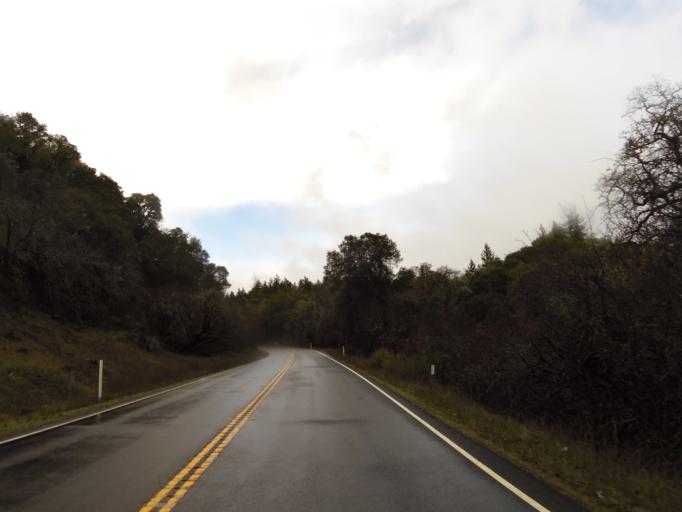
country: US
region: California
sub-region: Mendocino County
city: Boonville
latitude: 38.8952
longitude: -123.2082
